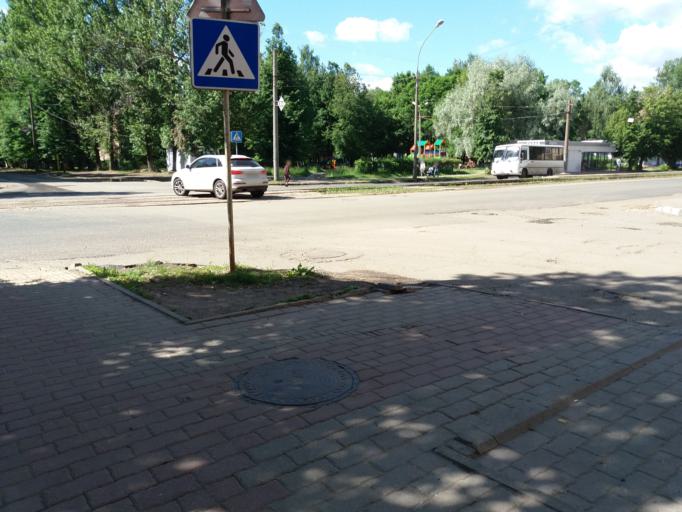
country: RU
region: Jaroslavl
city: Yaroslavl
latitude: 57.6381
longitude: 39.8303
